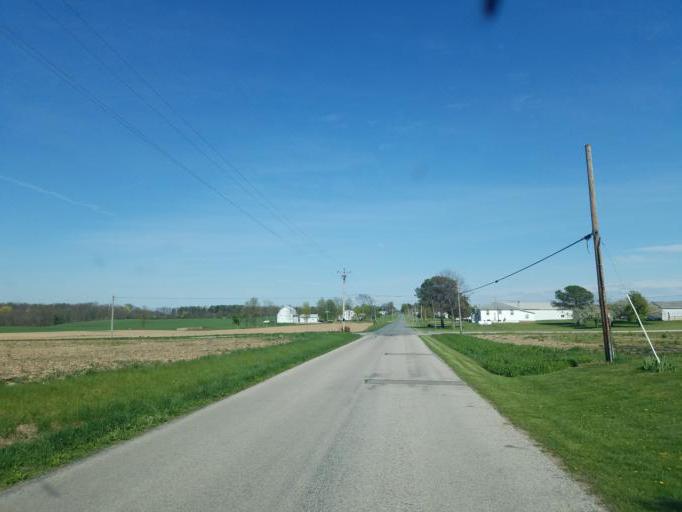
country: US
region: Ohio
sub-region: Huron County
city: Willard
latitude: 41.0835
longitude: -82.7685
